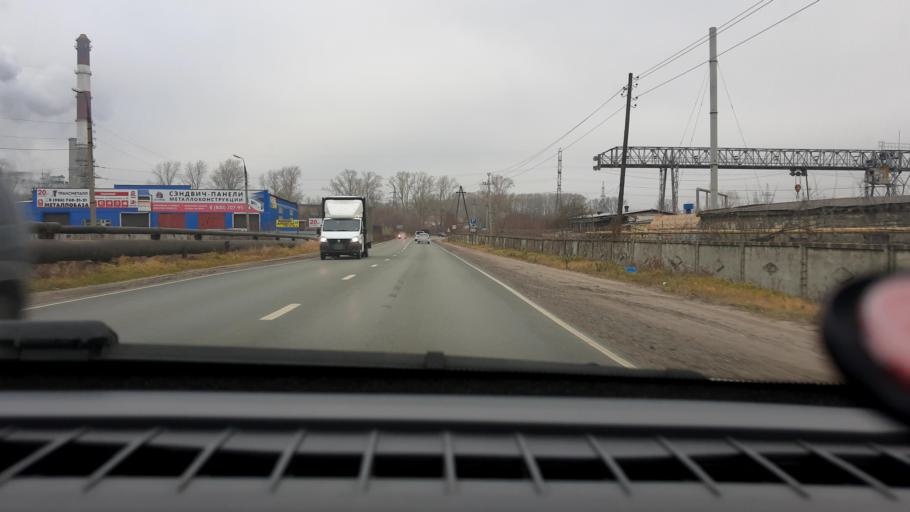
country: RU
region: Nizjnij Novgorod
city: Novaya Balakhna
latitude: 56.4967
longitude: 43.5943
